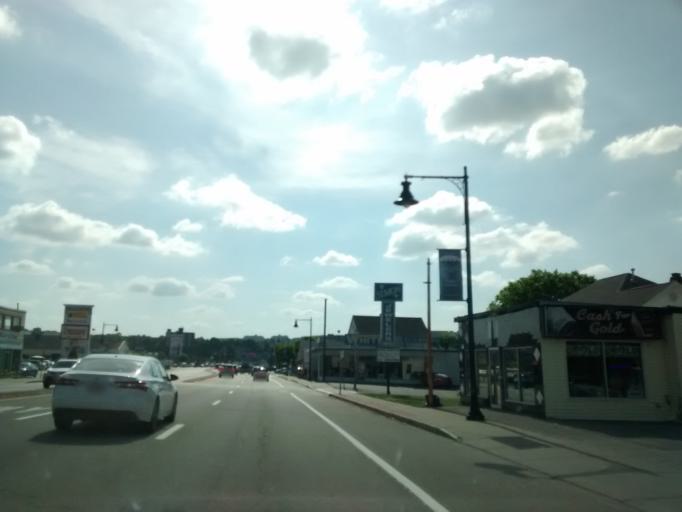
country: US
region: Massachusetts
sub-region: Worcester County
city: Hamilton
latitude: 42.2749
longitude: -71.7486
